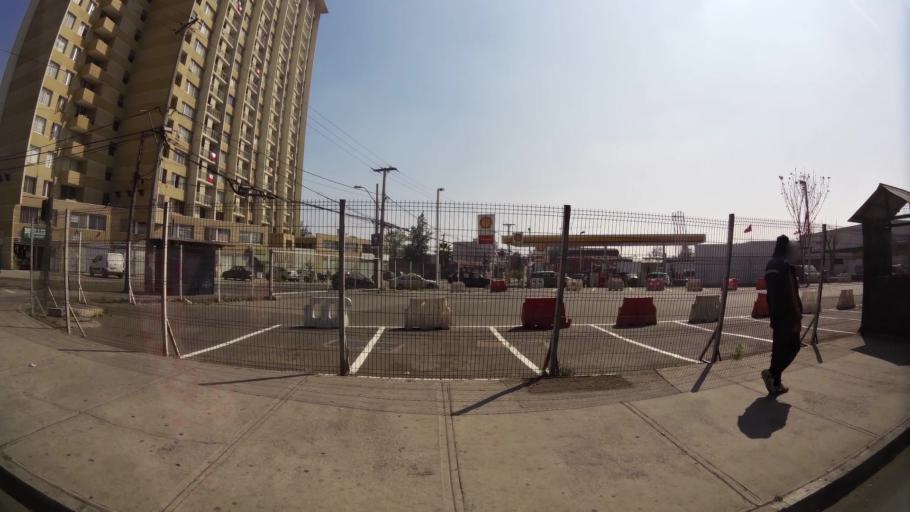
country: CL
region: Santiago Metropolitan
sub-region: Provincia de Santiago
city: Lo Prado
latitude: -33.4313
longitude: -70.6925
